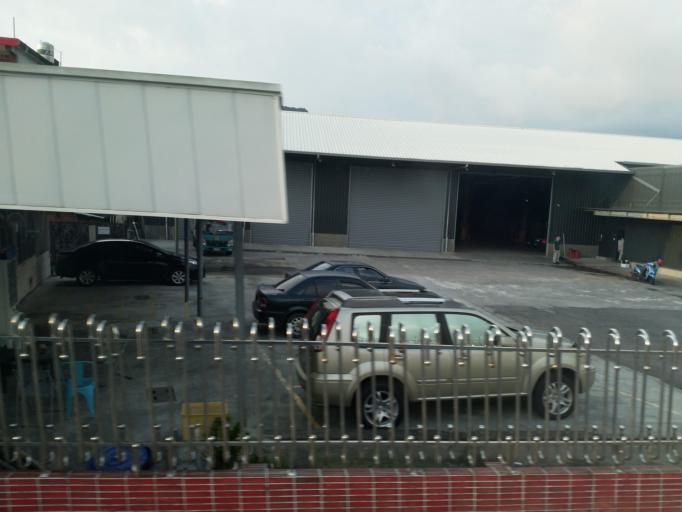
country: TW
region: Taiwan
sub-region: Pingtung
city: Pingtung
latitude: 22.8850
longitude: 120.5053
